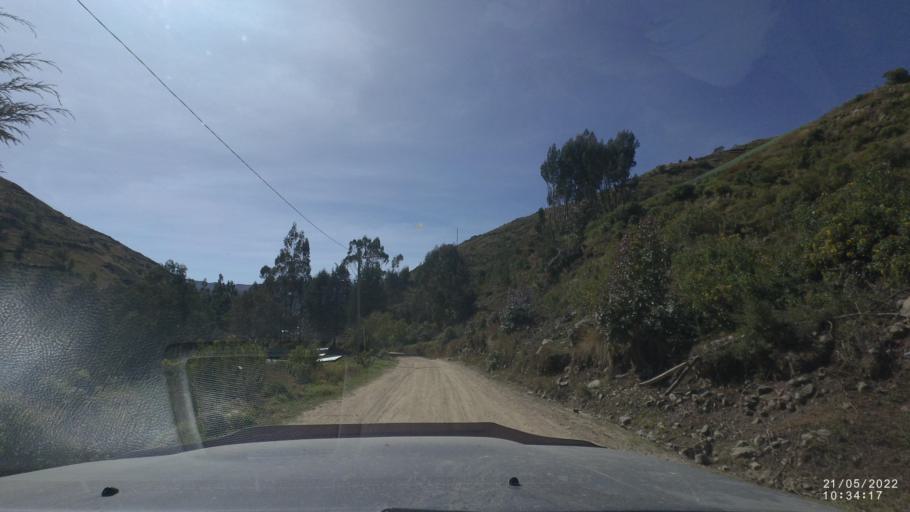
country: BO
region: Cochabamba
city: Colomi
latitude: -17.3208
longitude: -65.9322
